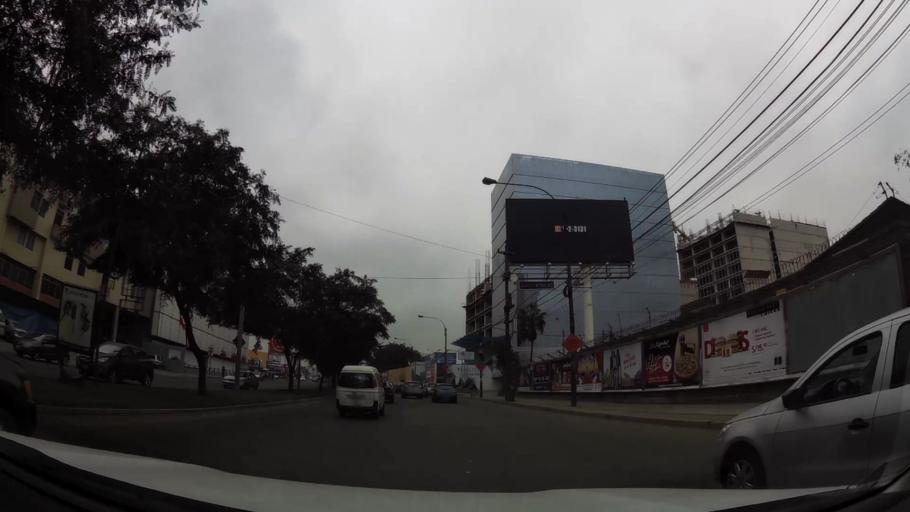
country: PE
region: Lima
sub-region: Lima
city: La Molina
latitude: -12.0809
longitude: -76.9668
